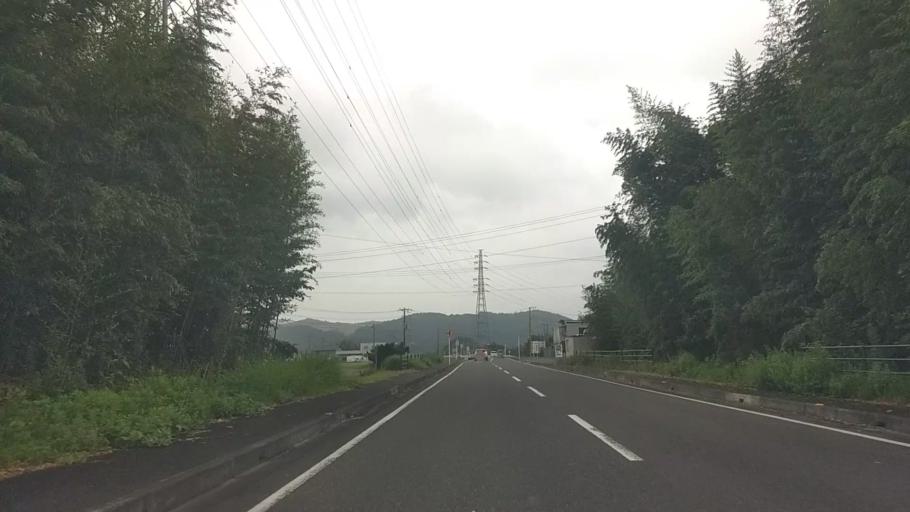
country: JP
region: Chiba
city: Kisarazu
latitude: 35.3120
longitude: 140.0595
